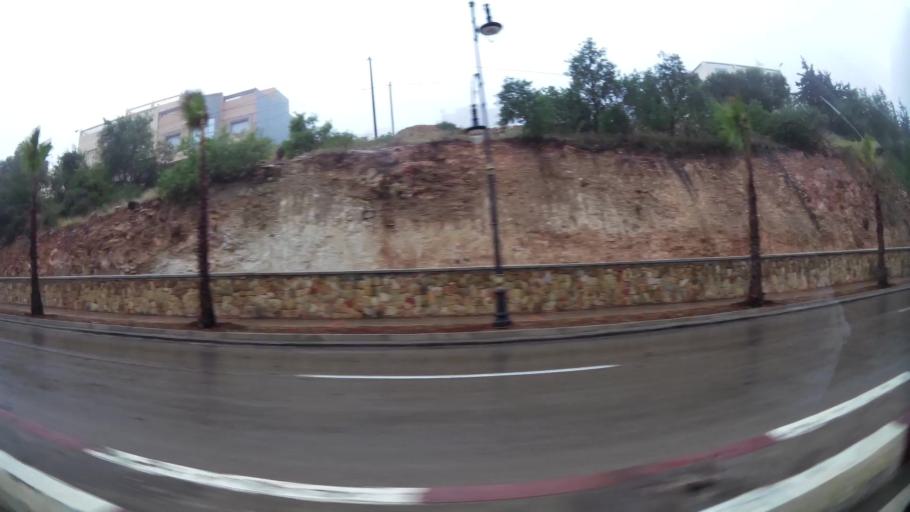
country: MA
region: Taza-Al Hoceima-Taounate
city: Tirhanimine
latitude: 35.2068
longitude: -3.9173
